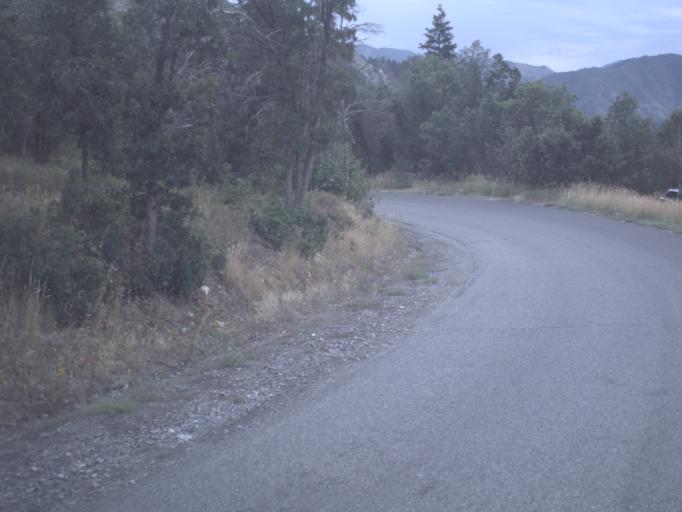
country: US
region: Utah
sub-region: Utah County
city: Lindon
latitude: 40.3969
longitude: -111.5894
